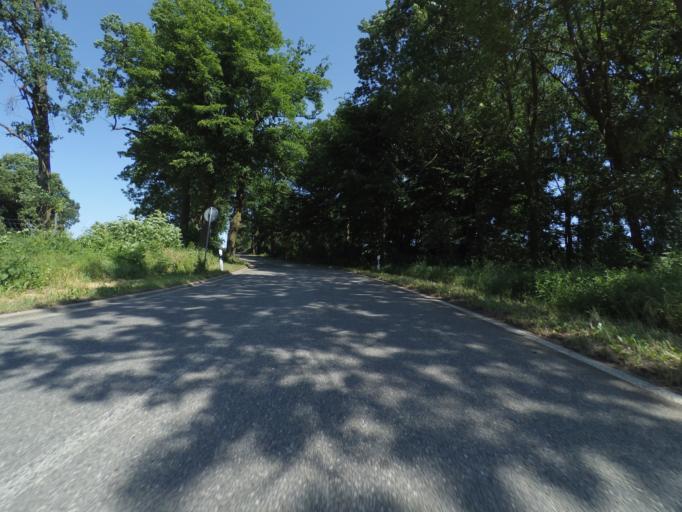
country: DE
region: Brandenburg
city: Heiligengrabe
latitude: 53.1670
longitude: 12.2854
